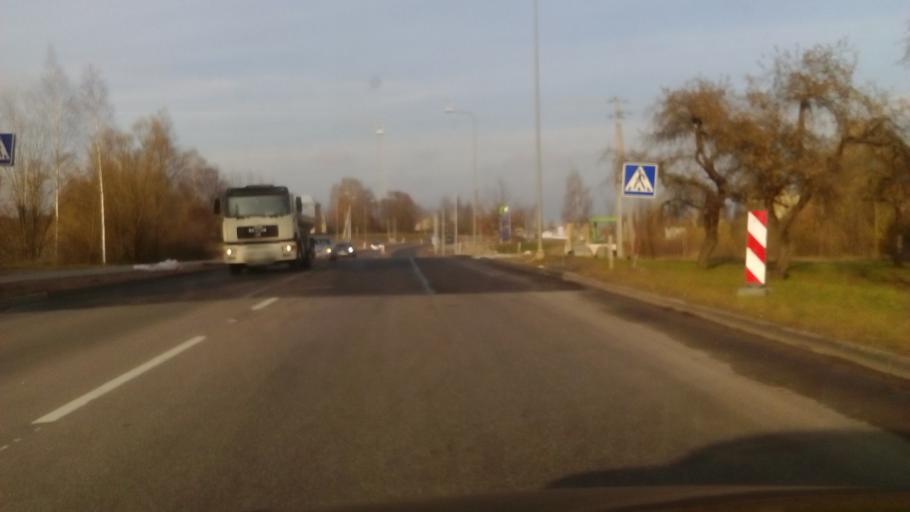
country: LT
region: Alytaus apskritis
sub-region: Alytus
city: Alytus
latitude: 54.4072
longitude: 24.0038
